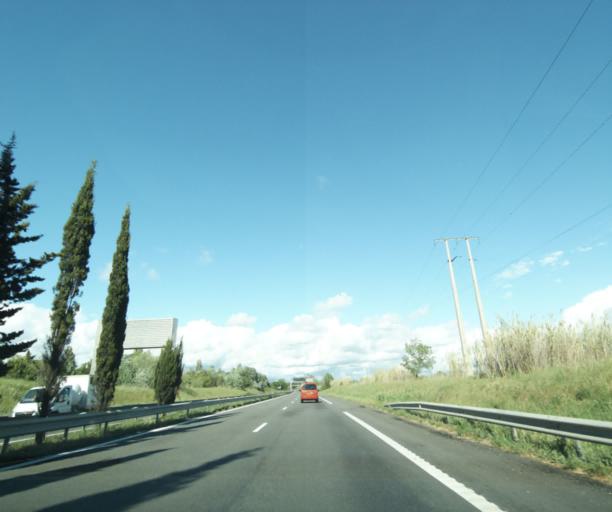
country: FR
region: Provence-Alpes-Cote d'Azur
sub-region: Departement des Bouches-du-Rhone
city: Saint-Martin-de-Crau
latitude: 43.6329
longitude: 4.8223
